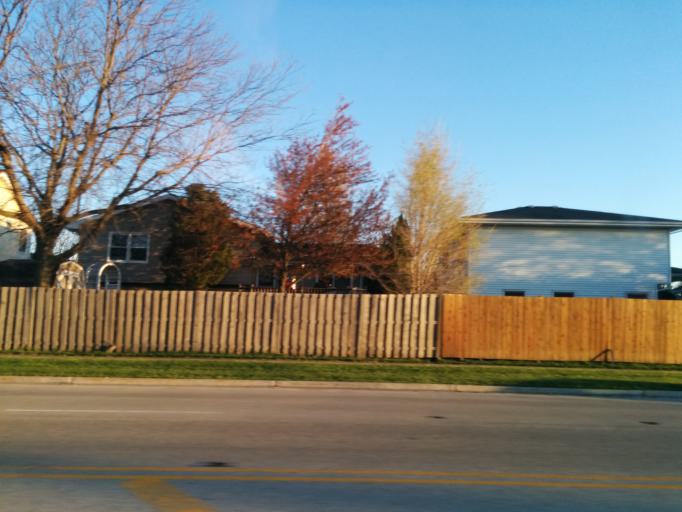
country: US
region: Illinois
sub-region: DuPage County
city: Hanover Park
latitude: 41.9738
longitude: -88.1538
